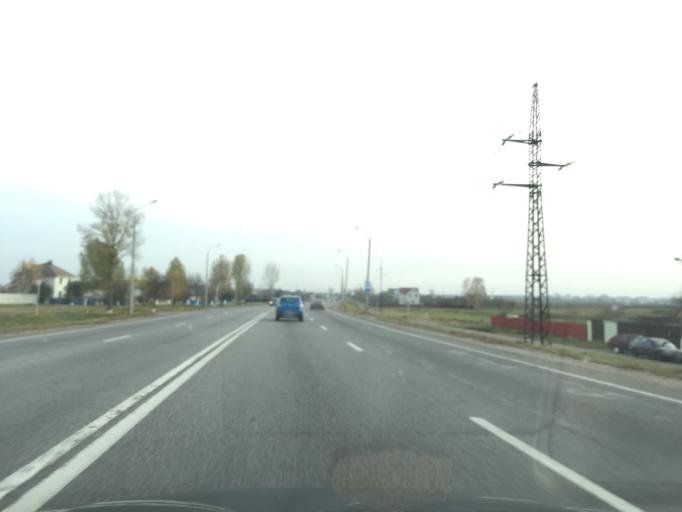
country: BY
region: Gomel
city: Kastsyukowka
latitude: 52.4983
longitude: 30.9565
